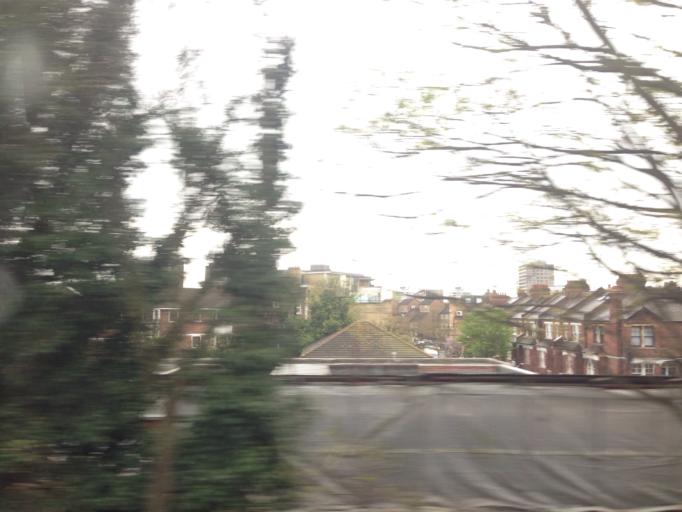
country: GB
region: England
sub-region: Greater London
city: Battersea
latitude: 51.4712
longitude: -0.1707
